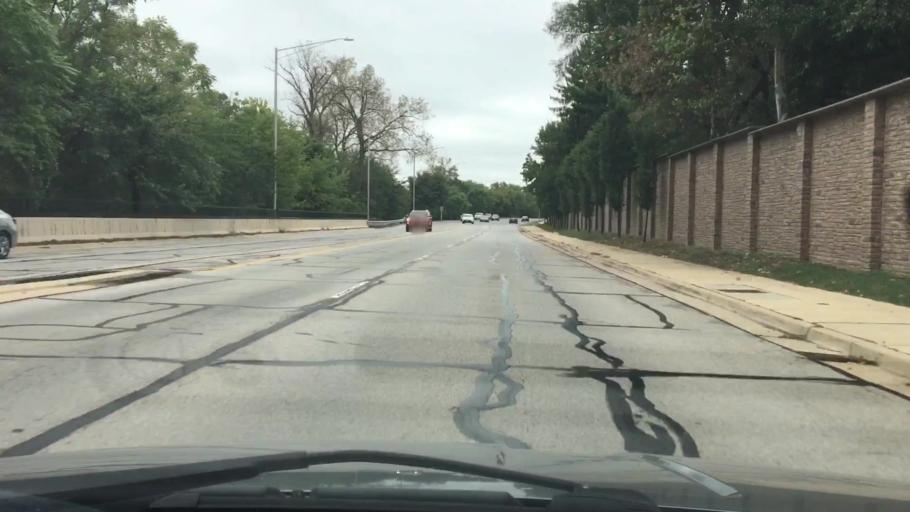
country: US
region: Illinois
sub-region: DuPage County
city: Naperville
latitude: 41.7459
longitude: -88.1288
